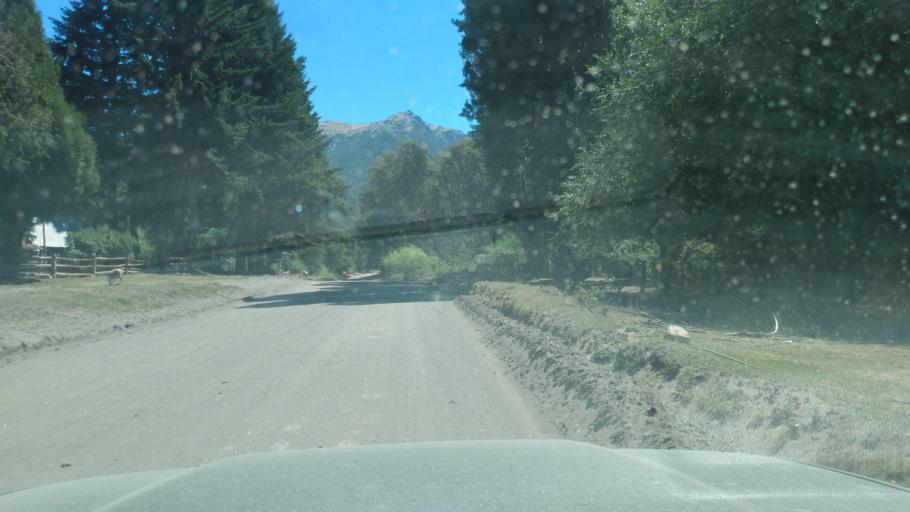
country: AR
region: Neuquen
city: Villa La Angostura
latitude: -40.6284
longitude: -71.4833
